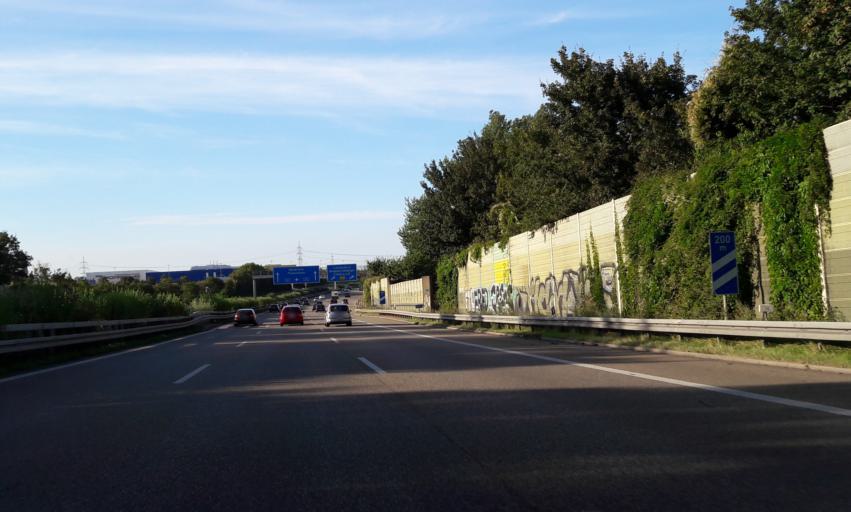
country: DE
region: Baden-Wuerttemberg
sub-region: Regierungsbezirk Stuttgart
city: Asperg
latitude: 48.9114
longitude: 9.1546
